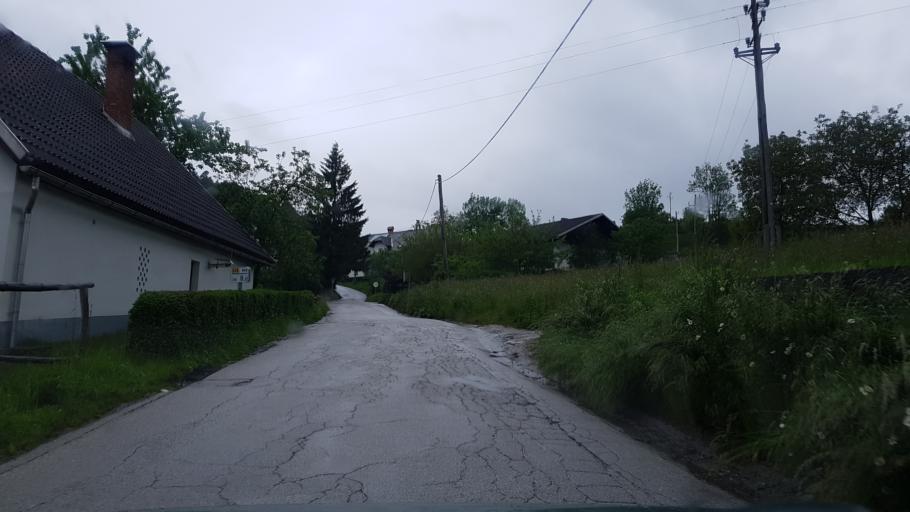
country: SI
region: Gorje
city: Zgornje Gorje
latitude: 46.3851
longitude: 14.0799
